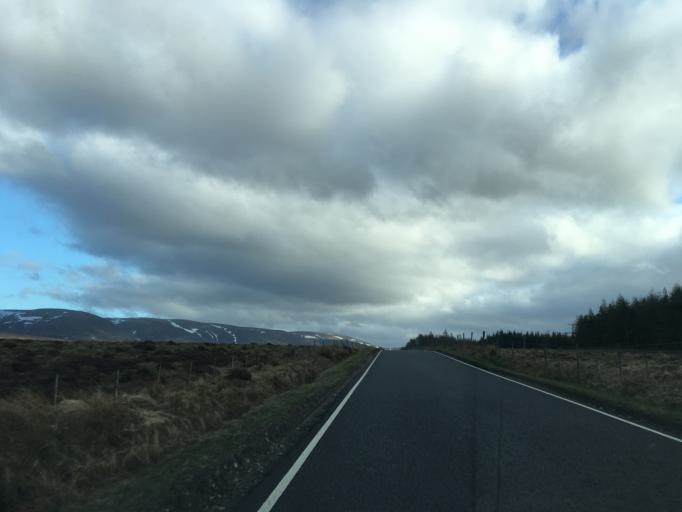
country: GB
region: Scotland
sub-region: Highland
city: Kingussie
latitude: 56.9558
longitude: -4.2444
